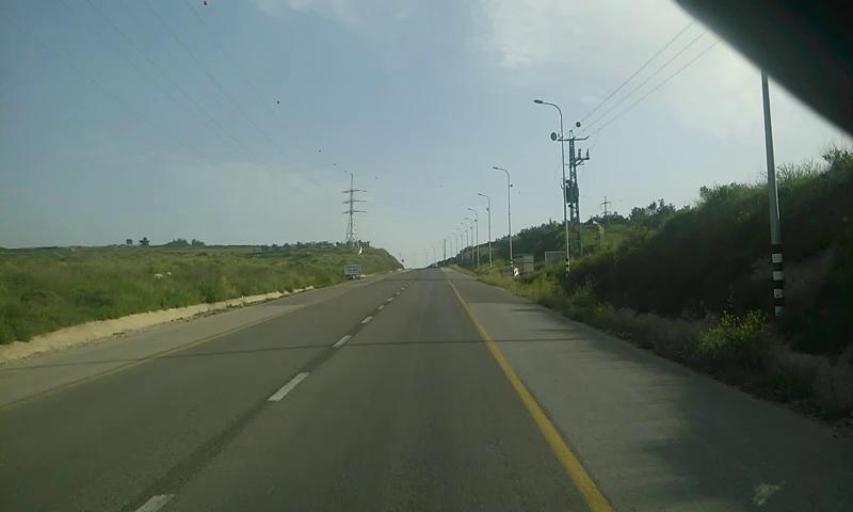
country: PS
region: West Bank
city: Sarrah
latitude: 32.2001
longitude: 35.1850
